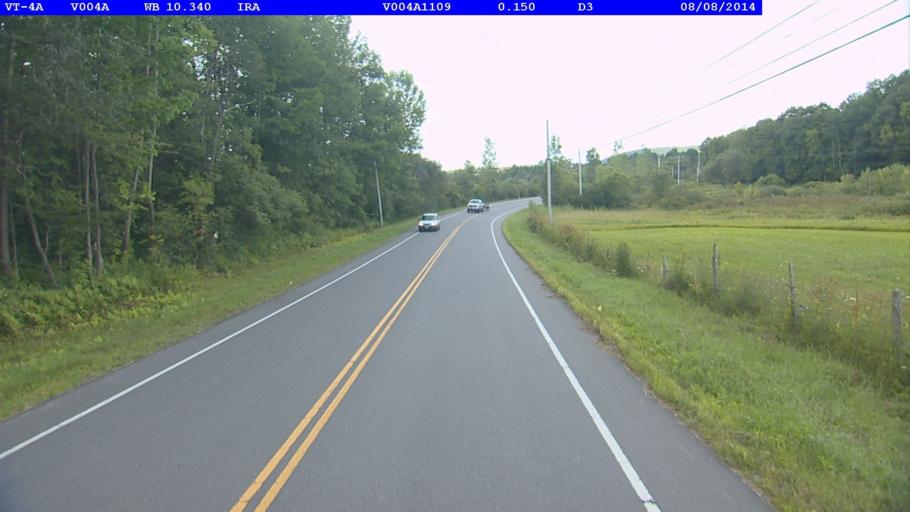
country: US
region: Vermont
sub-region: Rutland County
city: West Rutland
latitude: 43.6088
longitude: -73.1099
